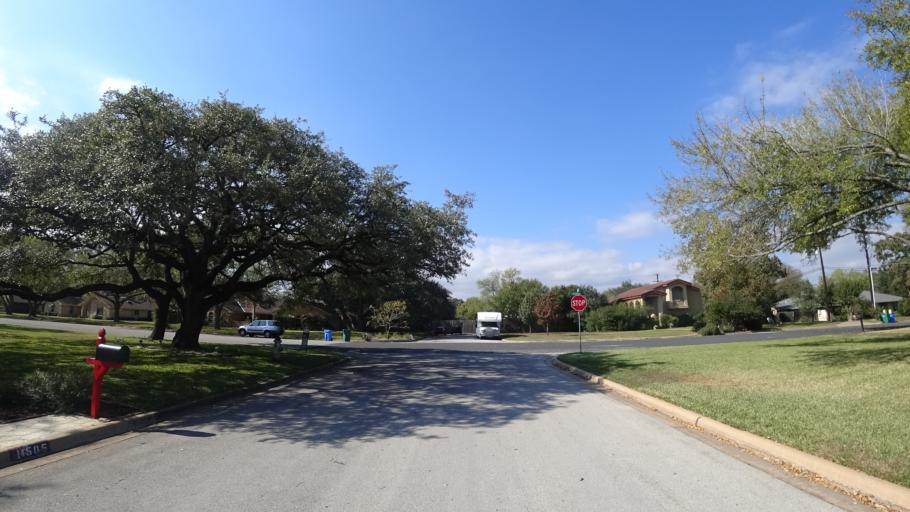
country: US
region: Texas
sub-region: Travis County
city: Shady Hollow
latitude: 30.1663
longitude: -97.8662
